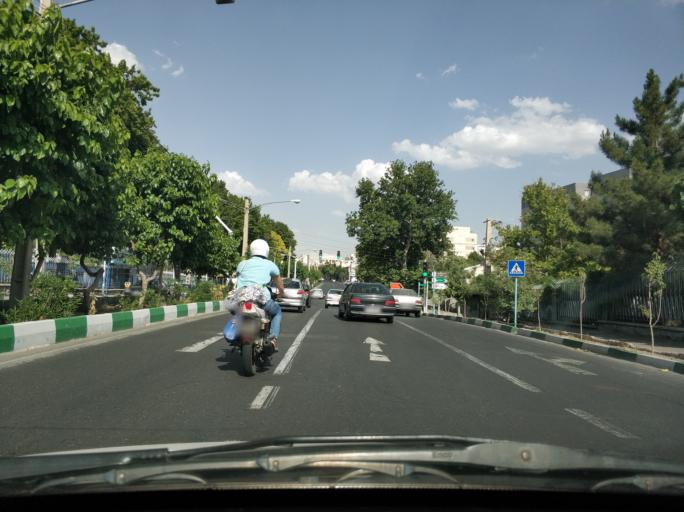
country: IR
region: Tehran
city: Tehran
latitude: 35.7425
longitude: 51.5846
